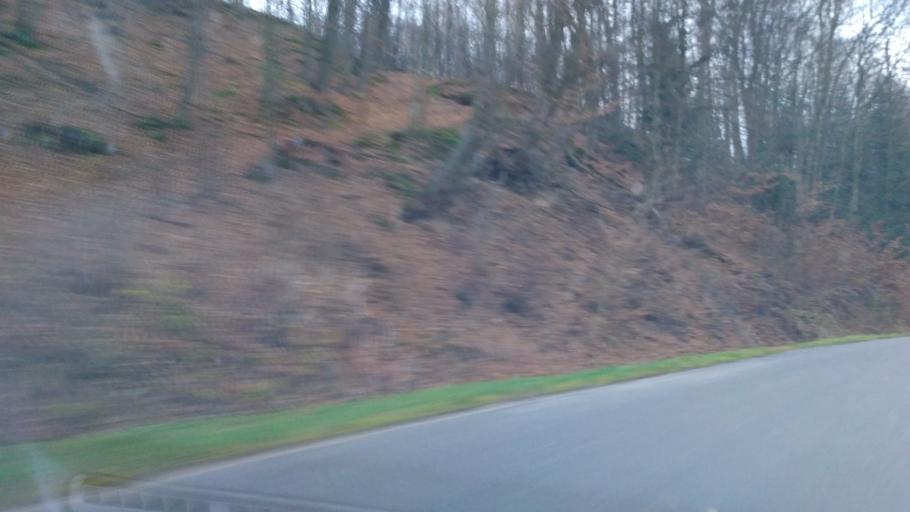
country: PL
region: Subcarpathian Voivodeship
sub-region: Powiat strzyzowski
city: Niebylec
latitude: 49.8657
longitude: 21.8878
